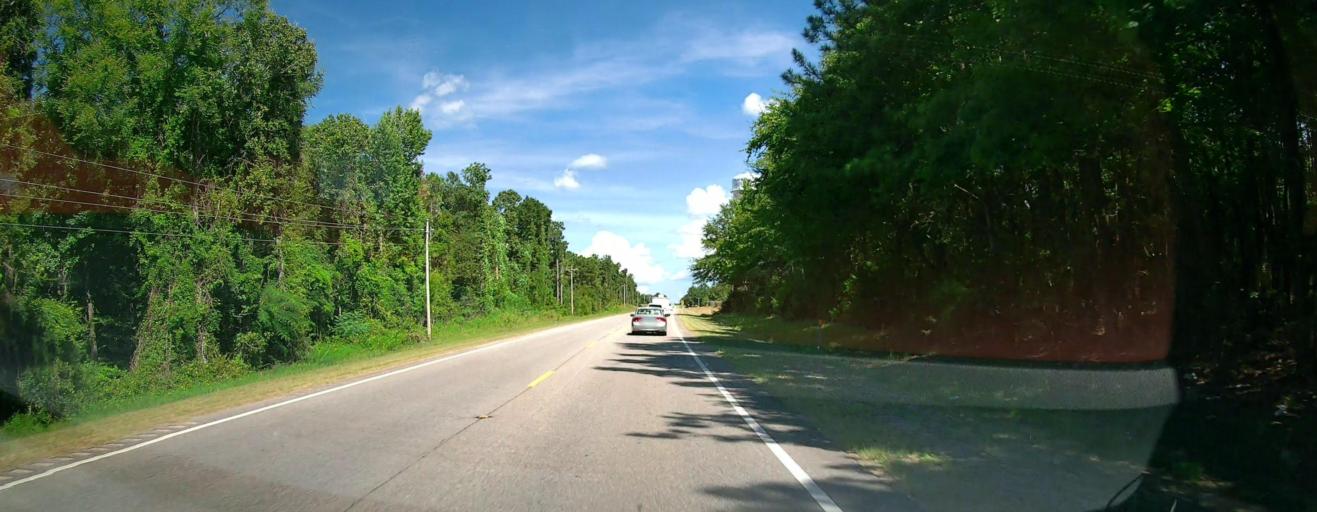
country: US
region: Alabama
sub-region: Elmore County
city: Tallassee
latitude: 32.3973
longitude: -85.9130
